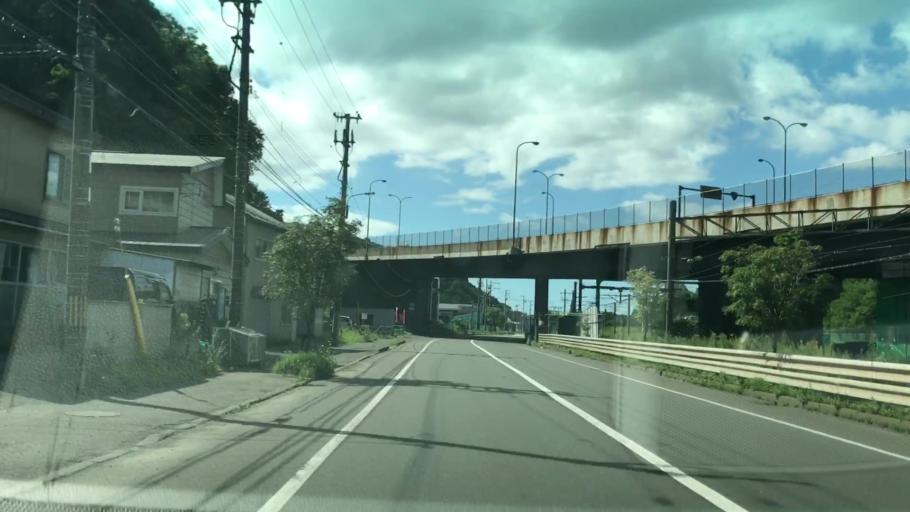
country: JP
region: Hokkaido
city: Muroran
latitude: 42.3335
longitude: 141.0038
